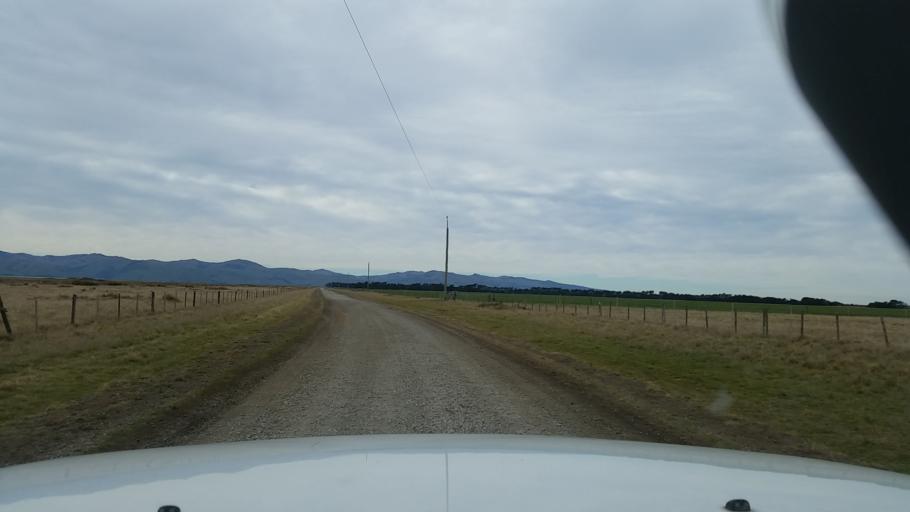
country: NZ
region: Canterbury
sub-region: Selwyn District
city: Lincoln
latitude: -43.8349
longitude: 172.4960
